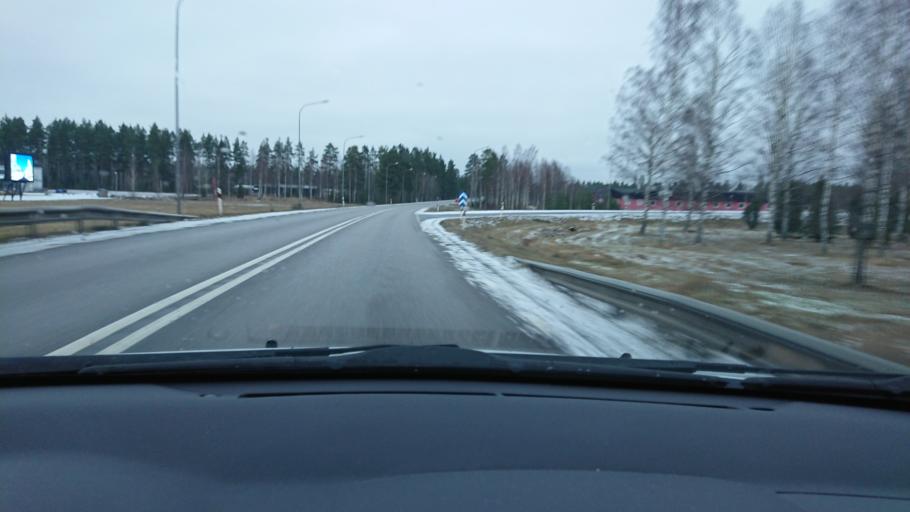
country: SE
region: Kalmar
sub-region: Hultsfreds Kommun
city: Hultsfred
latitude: 57.5006
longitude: 15.8218
